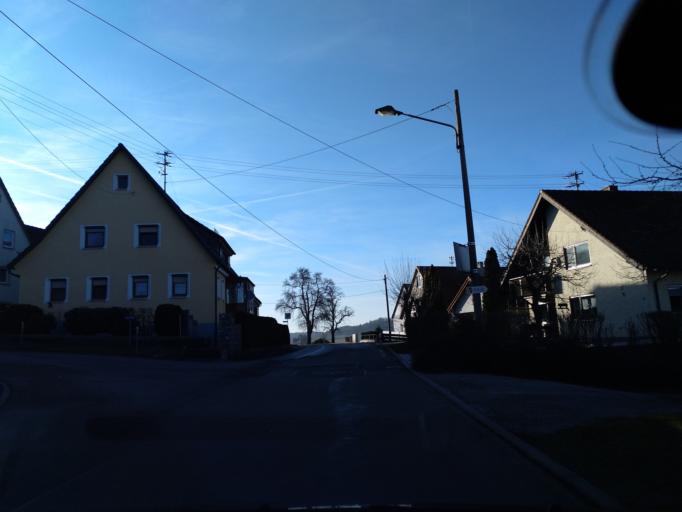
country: DE
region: Baden-Wuerttemberg
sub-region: Regierungsbezirk Stuttgart
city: Crailsheim
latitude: 49.0932
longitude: 10.0588
